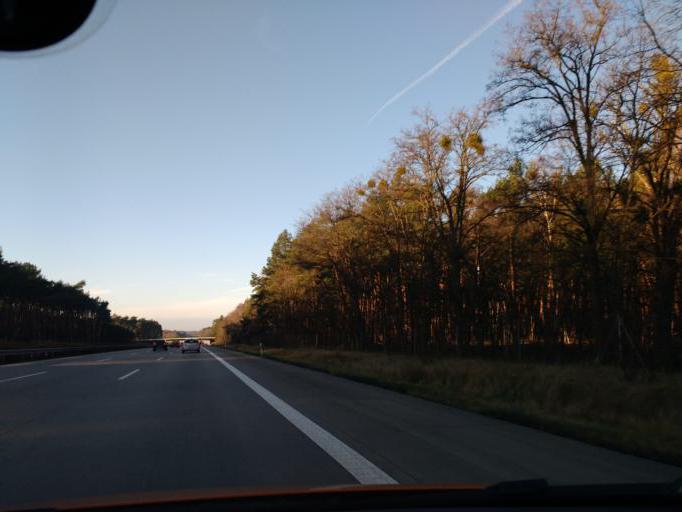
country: DE
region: Saxony-Anhalt
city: Mockern
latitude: 52.2344
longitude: 12.0193
